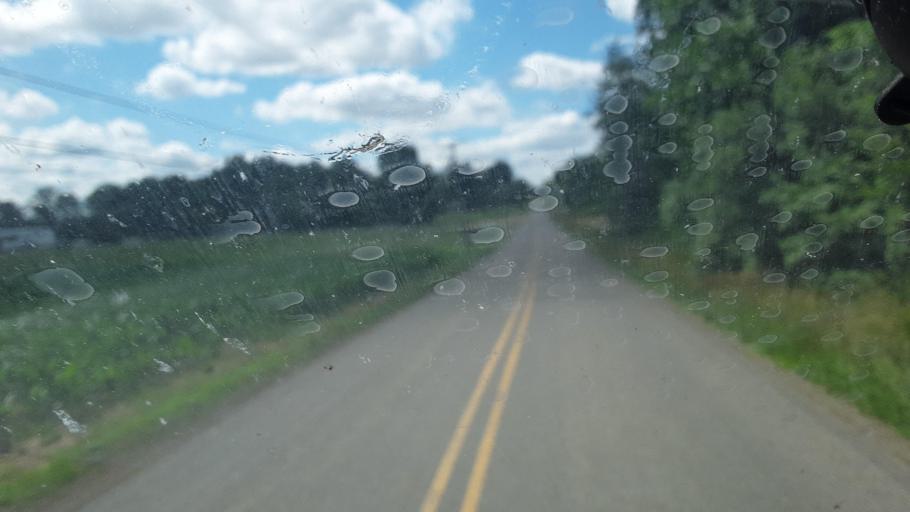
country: US
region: Pennsylvania
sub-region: Lawrence County
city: New Wilmington
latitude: 41.0542
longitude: -80.2339
